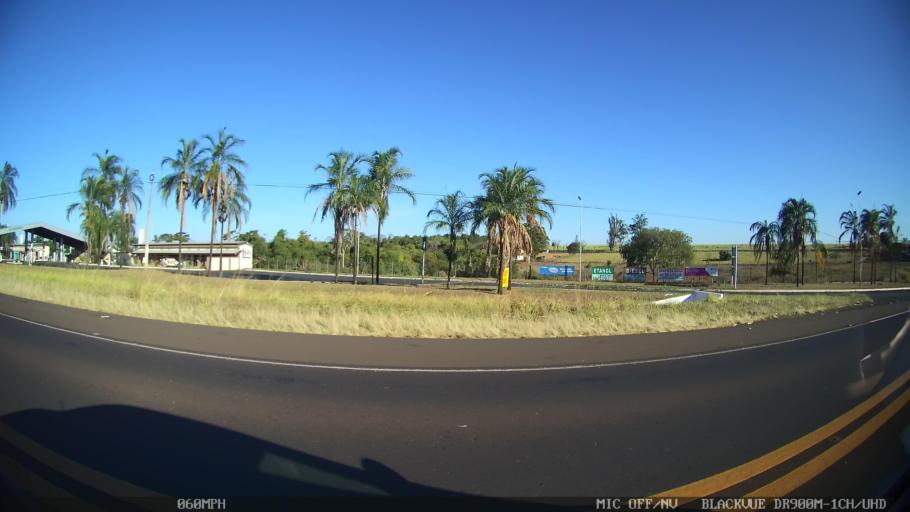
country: BR
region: Sao Paulo
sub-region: Olimpia
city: Olimpia
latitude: -20.7145
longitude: -48.9912
